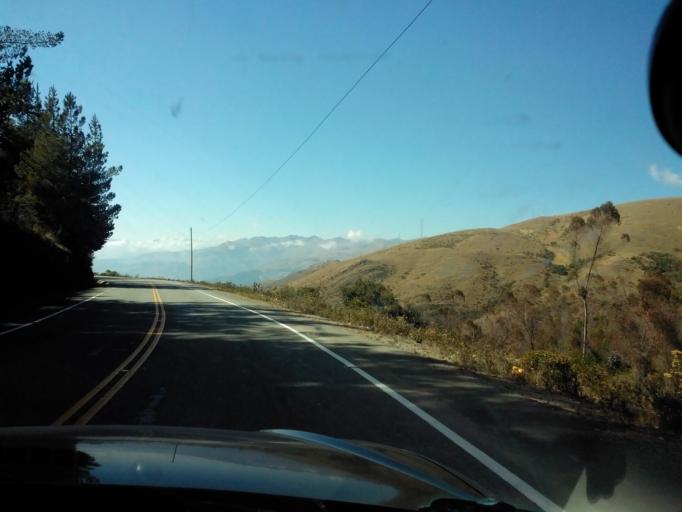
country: PE
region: Apurimac
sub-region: Provincia de Abancay
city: Cachora
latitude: -13.5564
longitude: -72.8197
